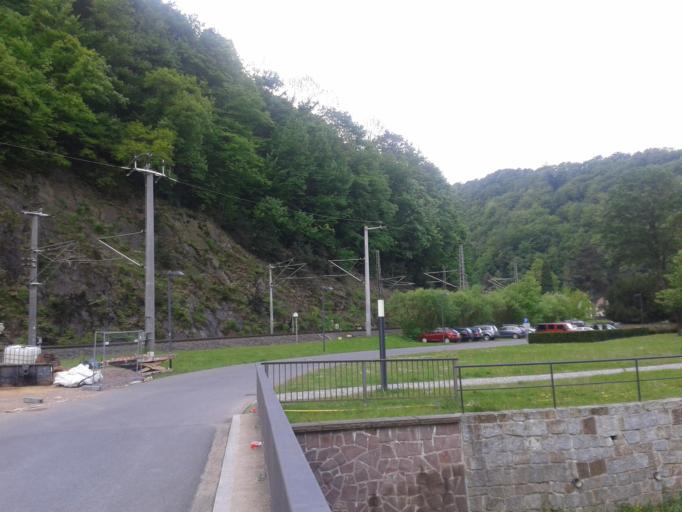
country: DE
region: Saxony
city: Tharandt
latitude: 50.9826
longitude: 13.5862
